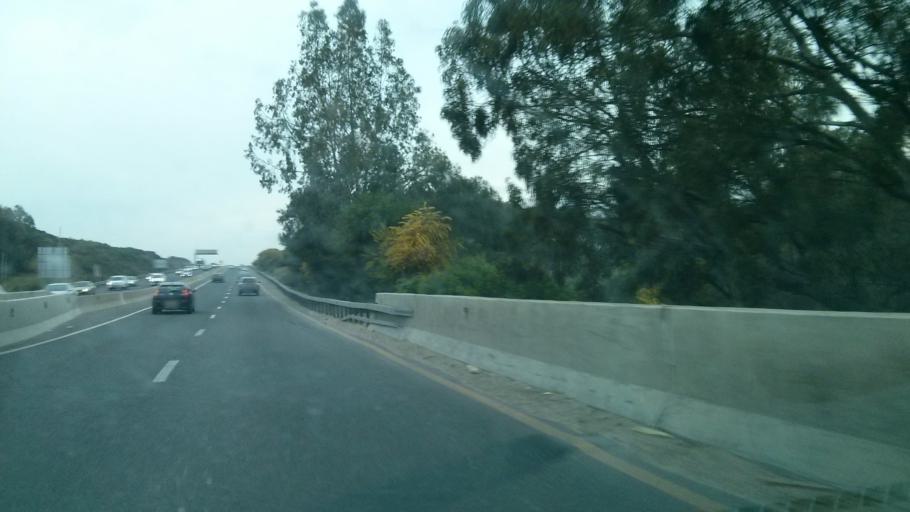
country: IL
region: Haifa
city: Hadera
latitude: 32.4665
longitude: 34.8969
